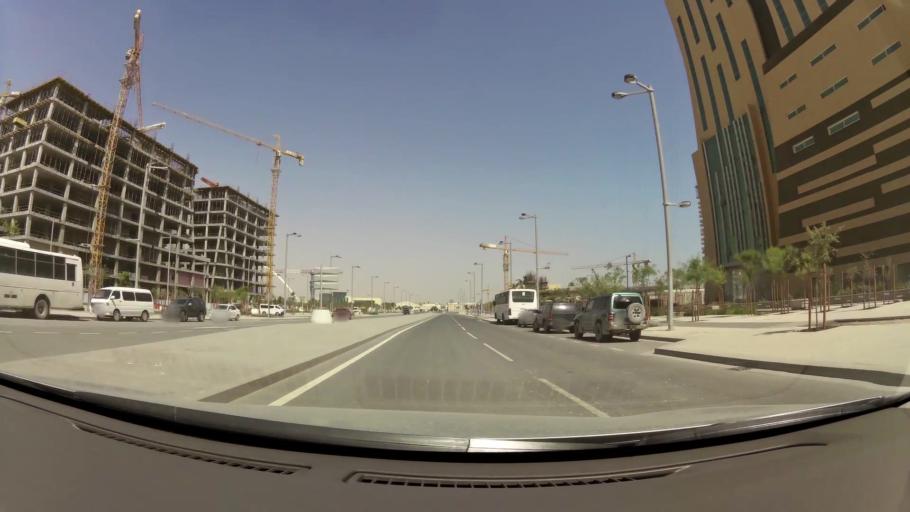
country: QA
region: Baladiyat ad Dawhah
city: Doha
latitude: 25.3957
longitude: 51.5200
